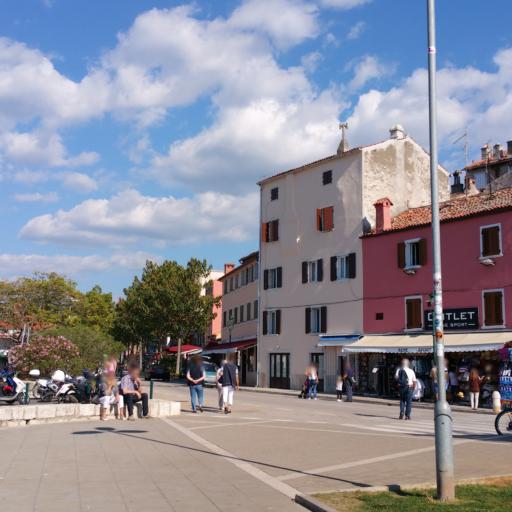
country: HR
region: Istarska
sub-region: Grad Rovinj
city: Rovinj
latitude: 45.0842
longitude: 13.6343
